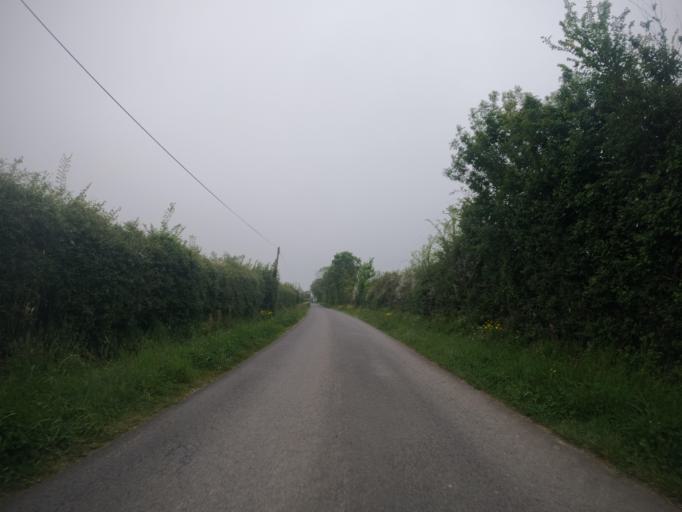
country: FR
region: Poitou-Charentes
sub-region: Departement des Deux-Sevres
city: Chiche
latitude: 46.8668
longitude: -0.3383
